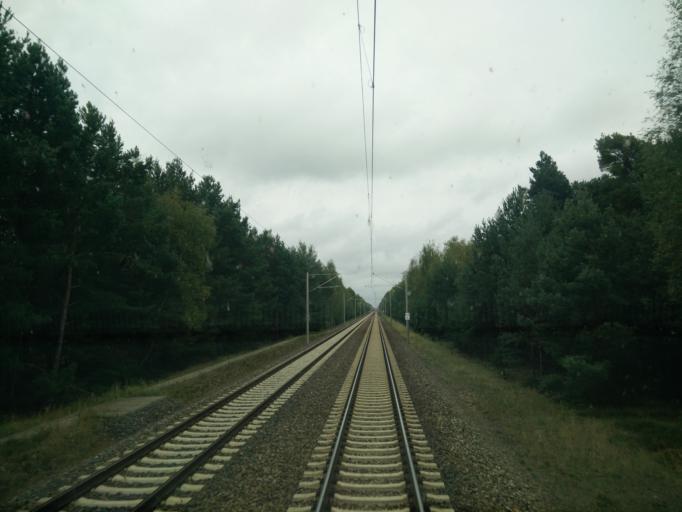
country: DE
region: Brandenburg
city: Kasel-Golzig
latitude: 52.0043
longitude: 13.7569
